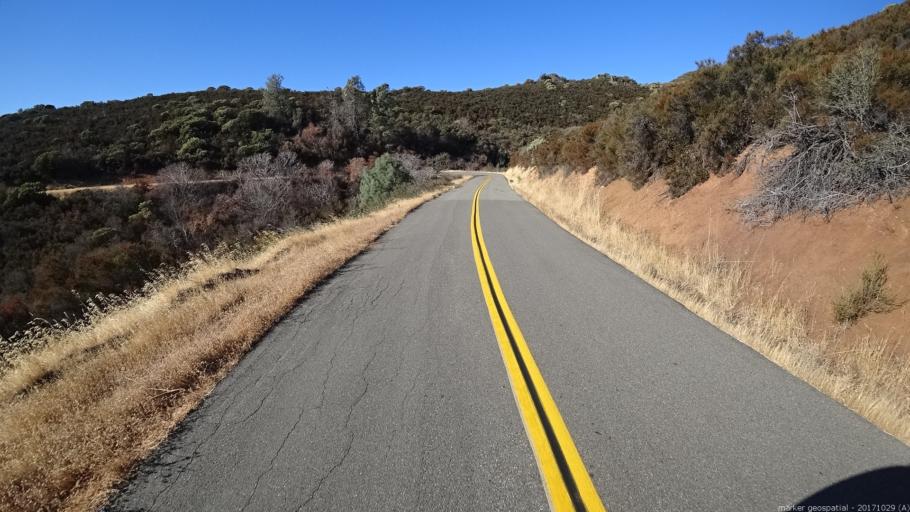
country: US
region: California
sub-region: Trinity County
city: Lewiston
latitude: 40.3660
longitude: -122.8574
